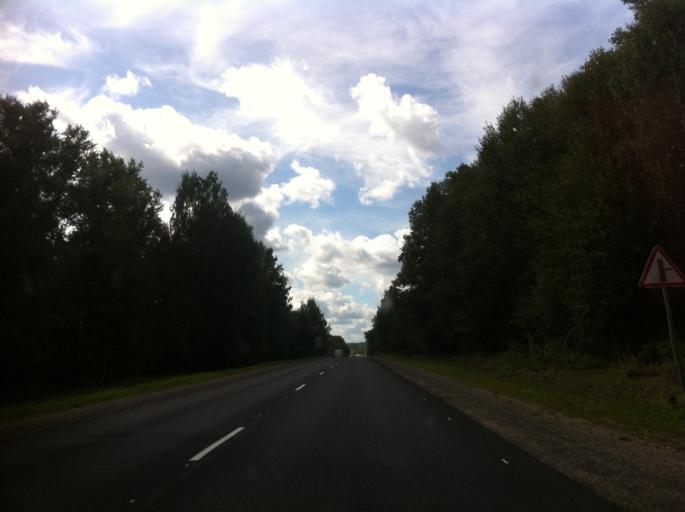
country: RU
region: Pskov
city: Izborsk
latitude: 57.7110
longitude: 27.8972
